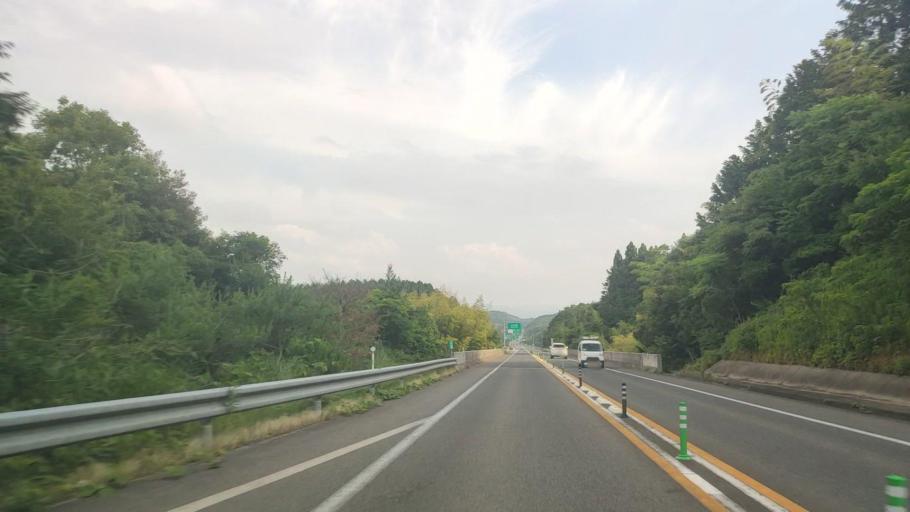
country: JP
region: Tottori
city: Kurayoshi
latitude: 35.4711
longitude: 133.8073
